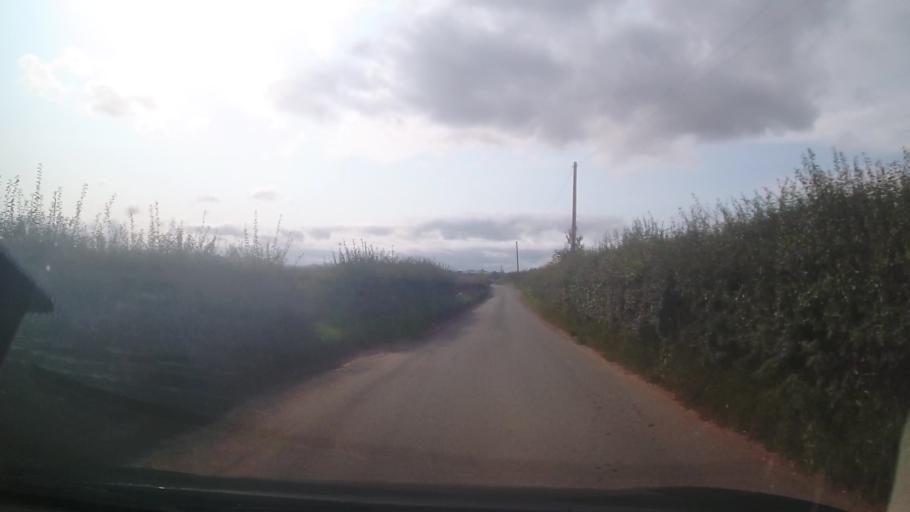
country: GB
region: England
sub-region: Shropshire
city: Bayston Hill
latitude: 52.6514
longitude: -2.7807
